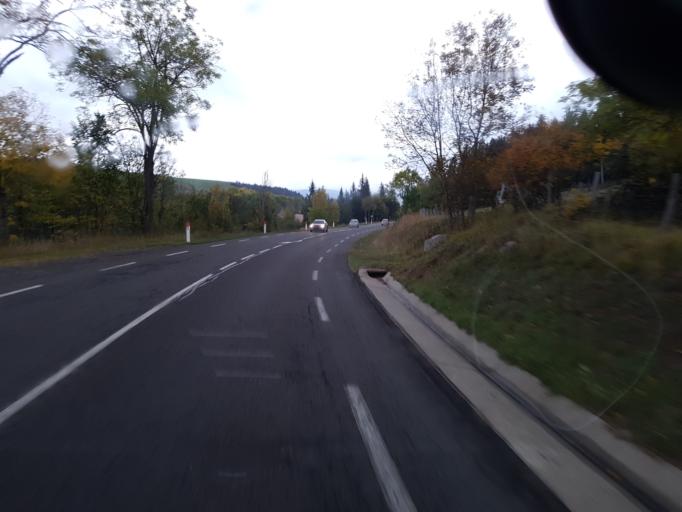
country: FR
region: Languedoc-Roussillon
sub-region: Departement de la Lozere
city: Mende
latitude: 44.5552
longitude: 3.6245
